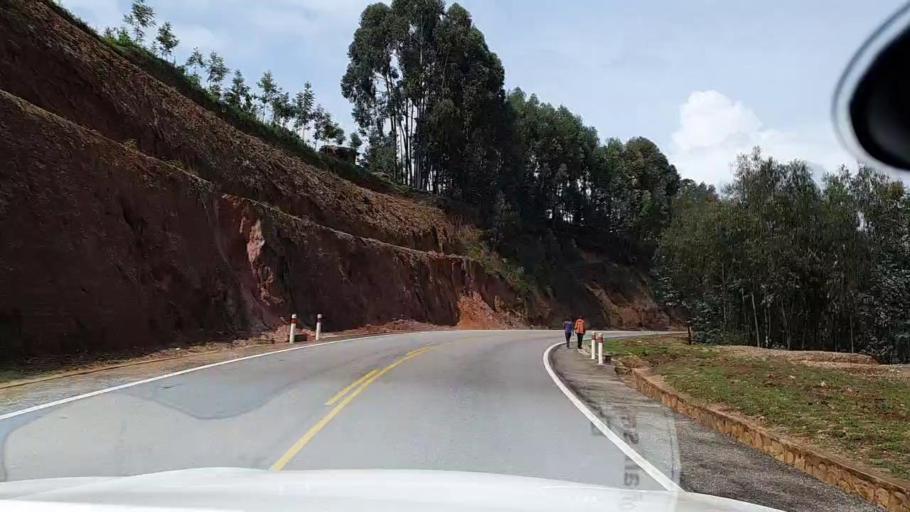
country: RW
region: Southern Province
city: Nzega
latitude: -2.4930
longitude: 29.5092
